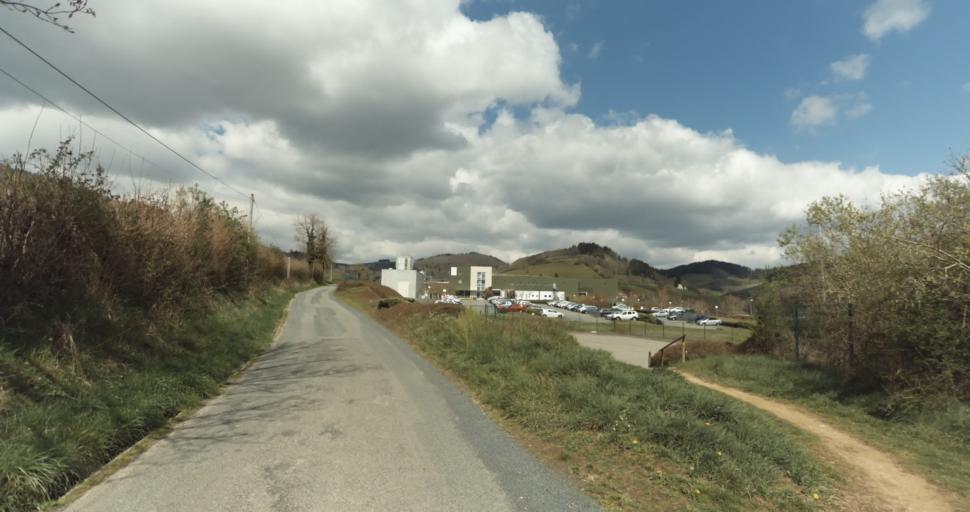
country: FR
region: Rhone-Alpes
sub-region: Departement du Rhone
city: Tarare
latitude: 45.9090
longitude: 4.4255
